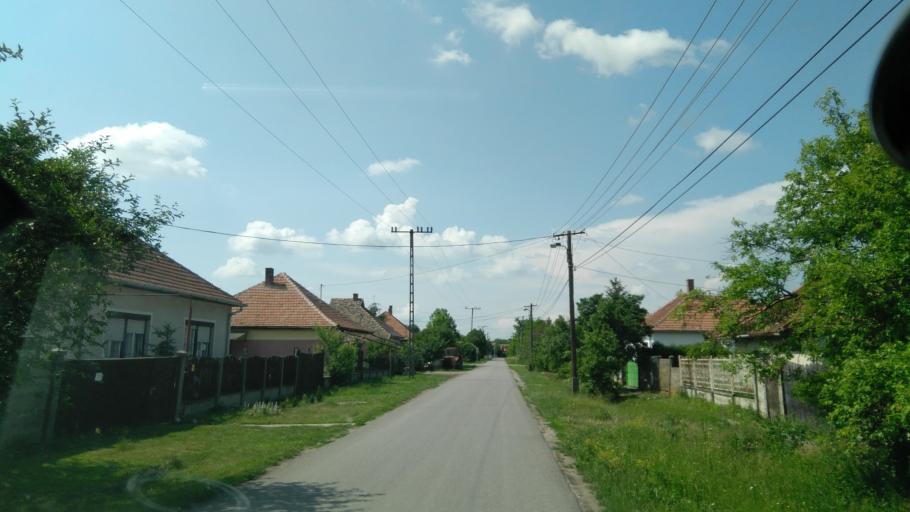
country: HU
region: Bekes
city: Doboz
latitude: 46.7346
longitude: 21.2312
